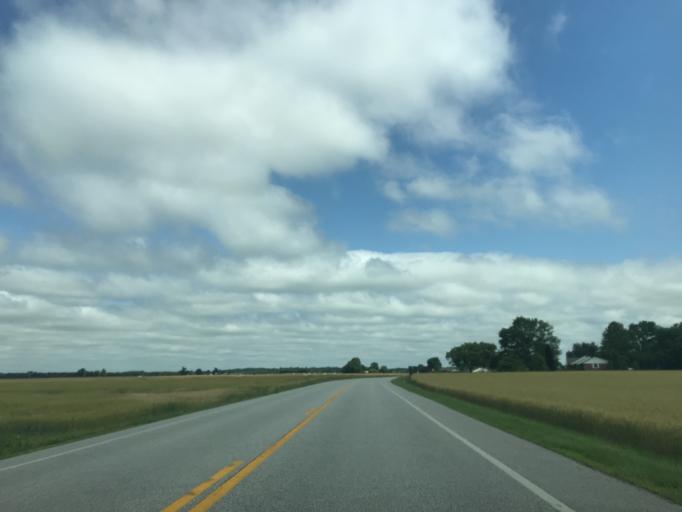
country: US
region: Maryland
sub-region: Caroline County
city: Ridgely
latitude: 38.9266
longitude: -75.8935
